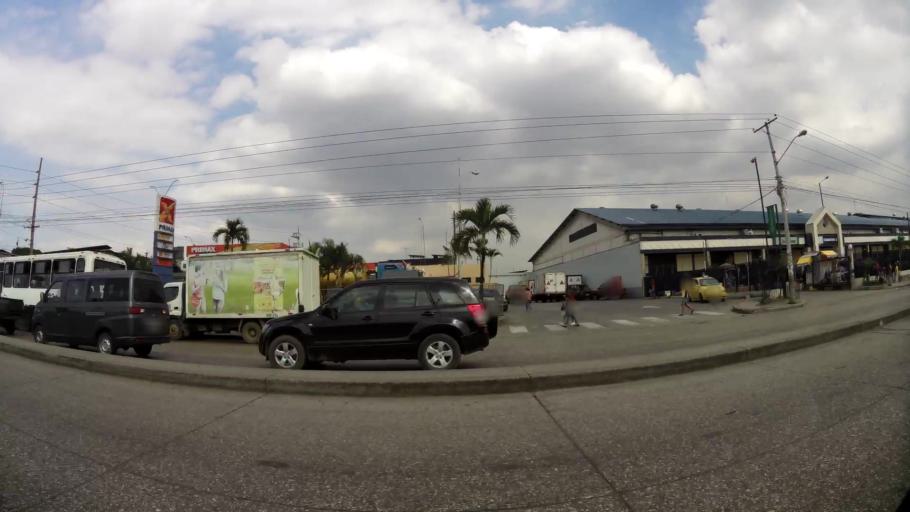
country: EC
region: Guayas
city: Santa Lucia
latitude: -2.0996
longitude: -79.9365
